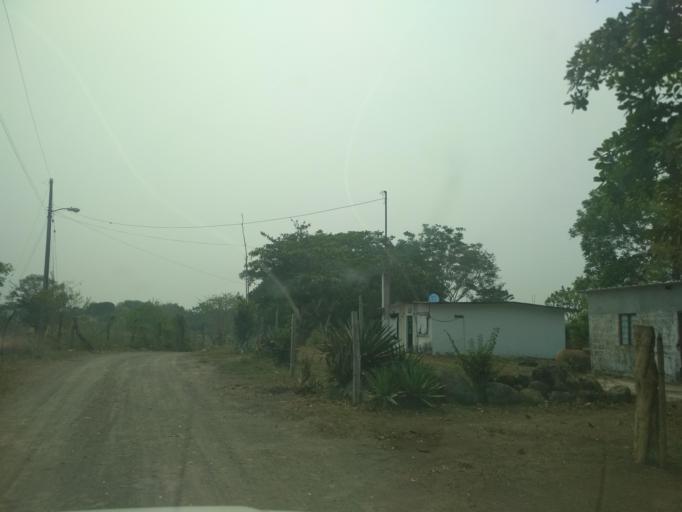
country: MX
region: Veracruz
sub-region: Veracruz
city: Delfino Victoria (Santa Fe)
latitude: 19.1806
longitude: -96.3264
